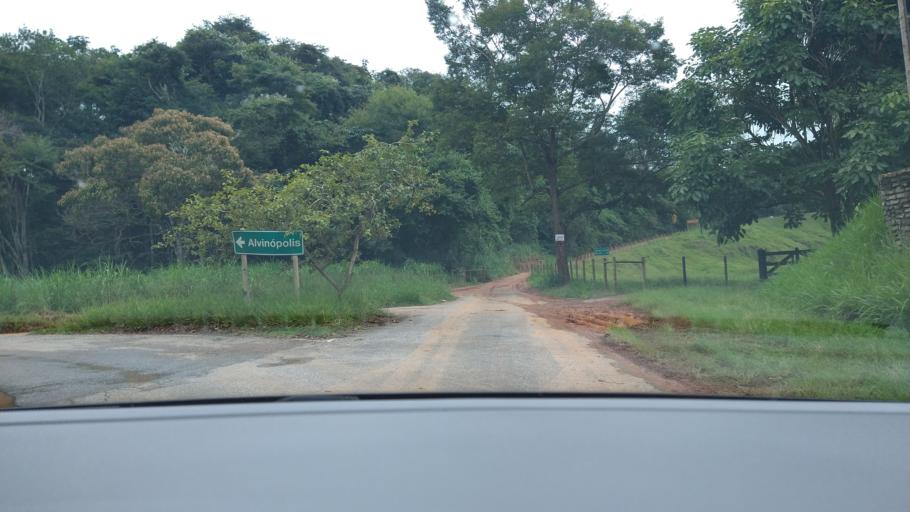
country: BR
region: Minas Gerais
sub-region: Alvinopolis
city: Alvinopolis
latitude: -20.1253
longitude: -42.9643
